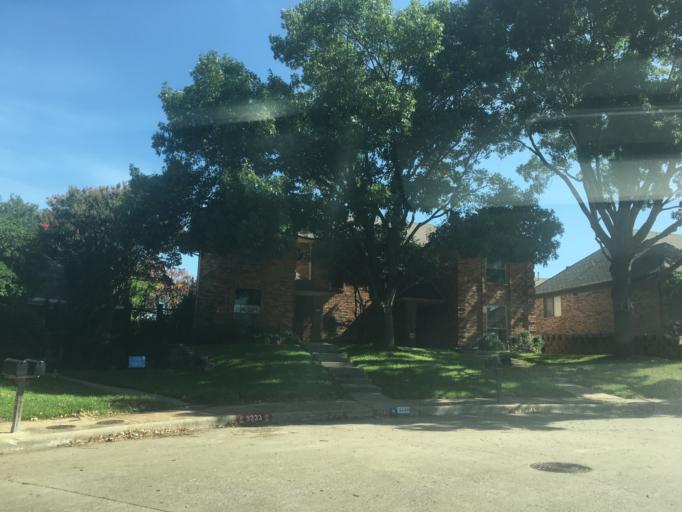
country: US
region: Texas
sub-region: Dallas County
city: Richardson
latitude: 32.8743
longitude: -96.7301
